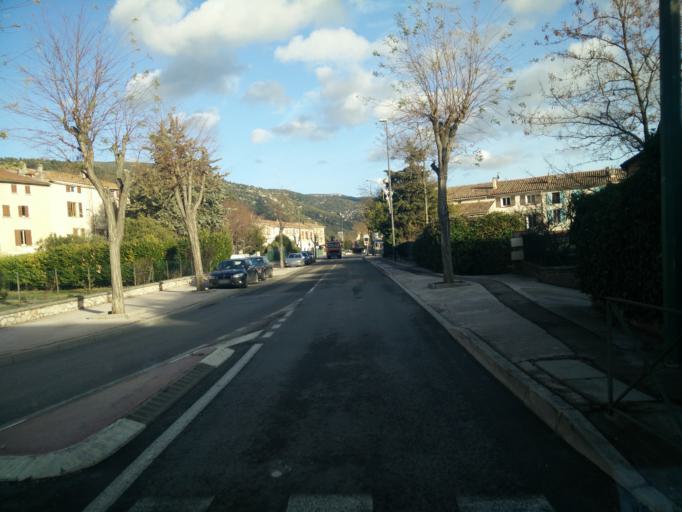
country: FR
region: Provence-Alpes-Cote d'Azur
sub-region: Departement du Var
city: Signes
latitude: 43.2903
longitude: 5.8636
